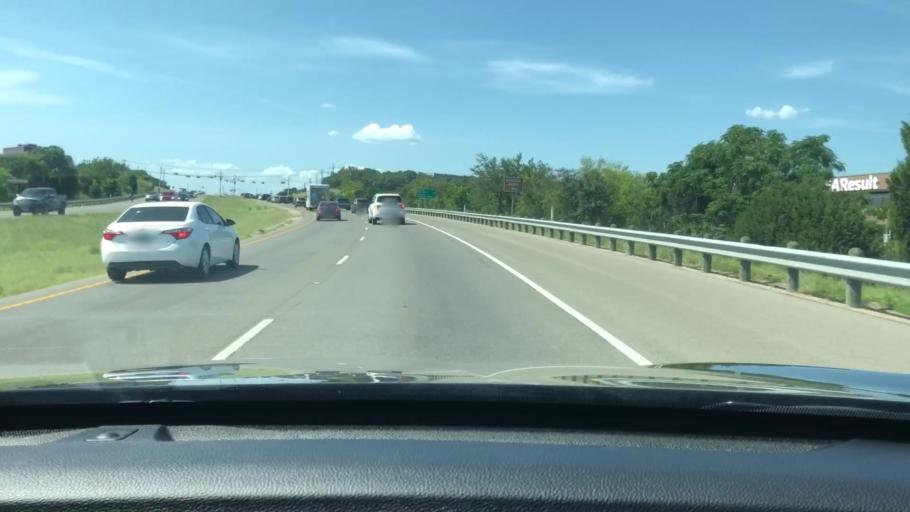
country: US
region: Texas
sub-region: Travis County
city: Rollingwood
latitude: 30.2752
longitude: -97.8174
